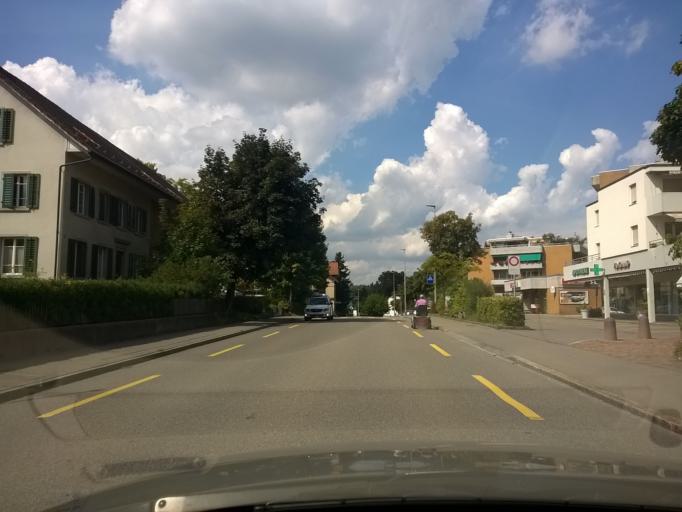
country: CH
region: Zurich
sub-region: Bezirk Buelach
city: Dietlikon / Eichwiesen
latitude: 47.4226
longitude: 8.6186
